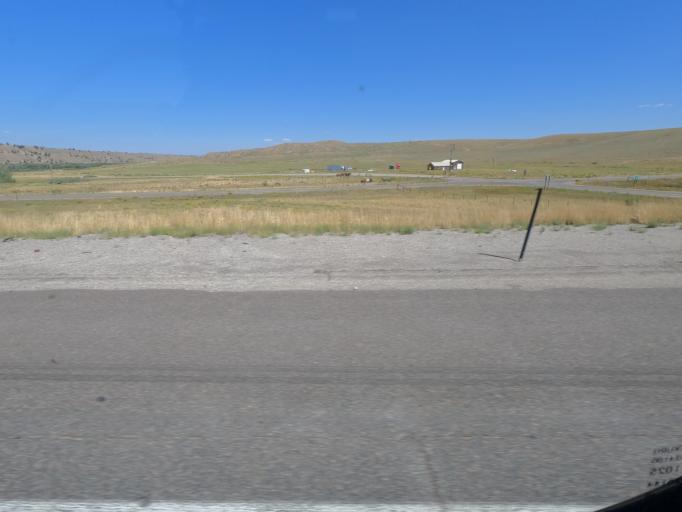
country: US
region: Wyoming
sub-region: Carbon County
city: Saratoga
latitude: 41.6964
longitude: -106.3830
